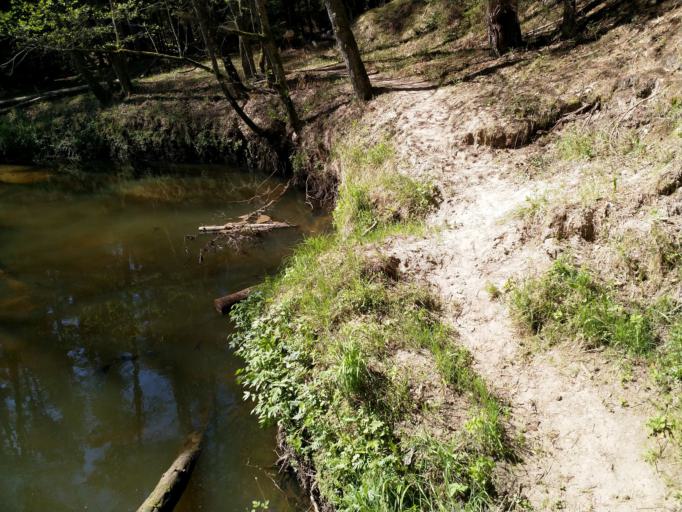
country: LV
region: Pavilostas
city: Pavilosta
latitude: 56.9601
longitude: 21.3547
